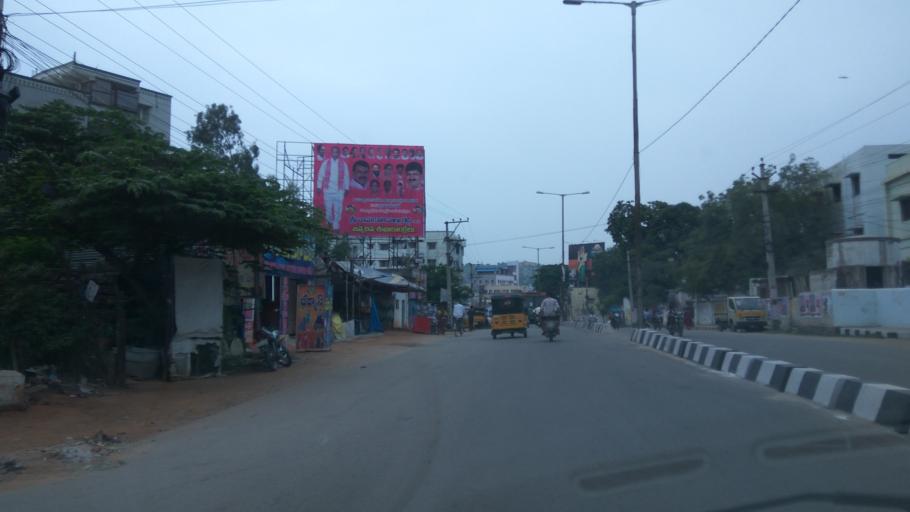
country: IN
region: Telangana
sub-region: Hyderabad
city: Malkajgiri
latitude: 17.4500
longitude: 78.5342
